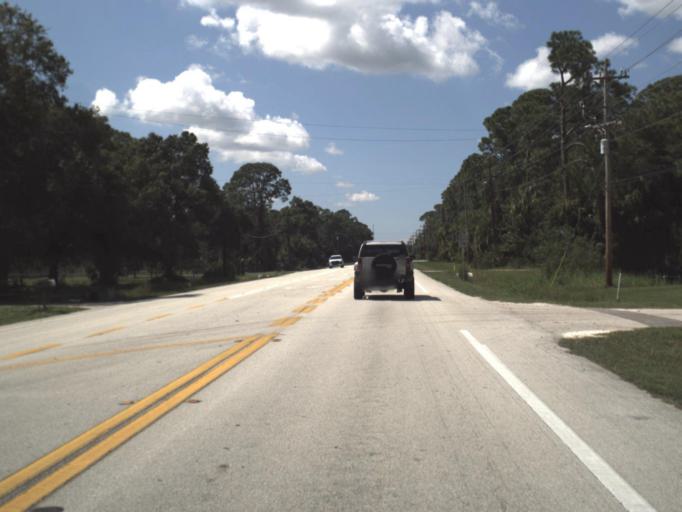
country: US
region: Florida
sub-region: Lee County
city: Fort Myers Shores
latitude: 26.7150
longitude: -81.7885
